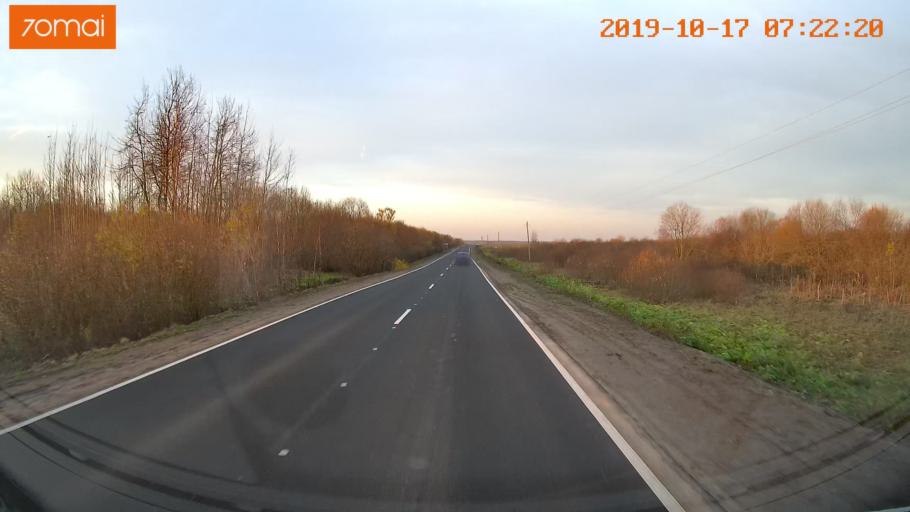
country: RU
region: Ivanovo
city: Gavrilov Posad
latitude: 56.3439
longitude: 40.1419
